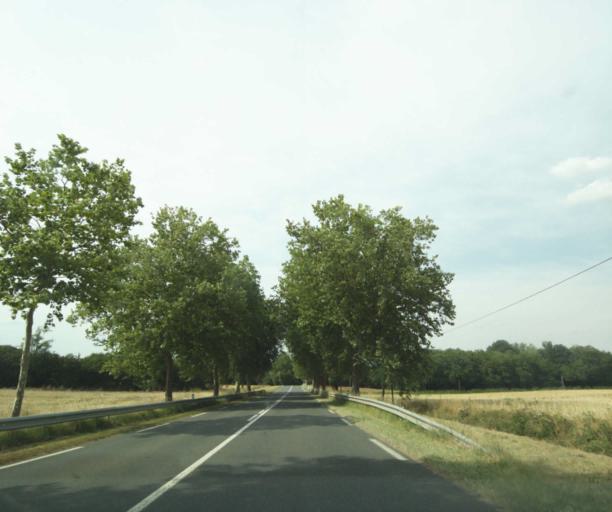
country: FR
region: Centre
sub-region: Departement d'Indre-et-Loire
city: Saint-Christophe-sur-le-Nais
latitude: 47.6256
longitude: 0.5040
